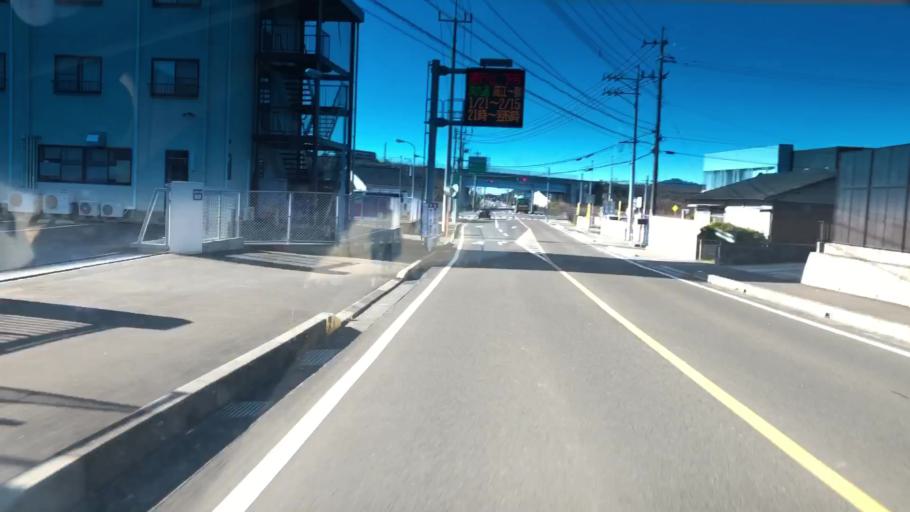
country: JP
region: Kagoshima
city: Satsumasendai
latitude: 31.8210
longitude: 130.2619
